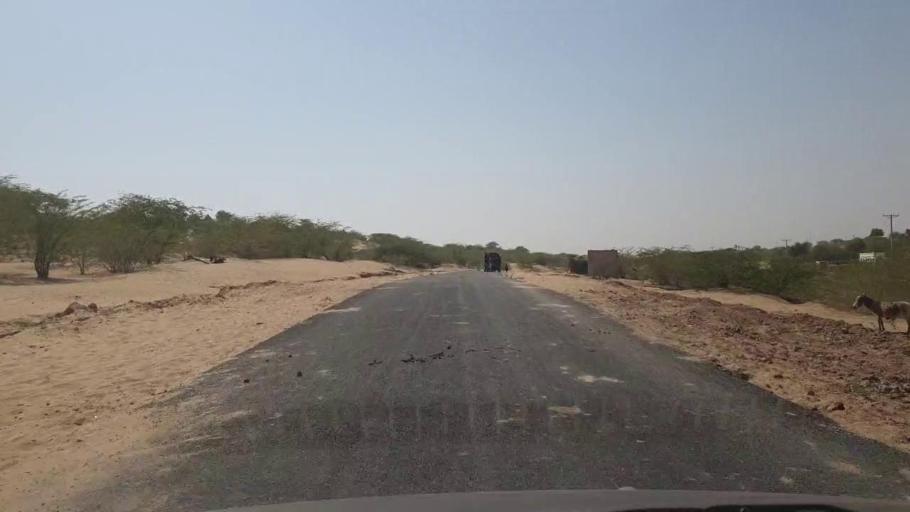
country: PK
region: Sindh
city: Chor
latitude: 25.5671
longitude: 70.1774
